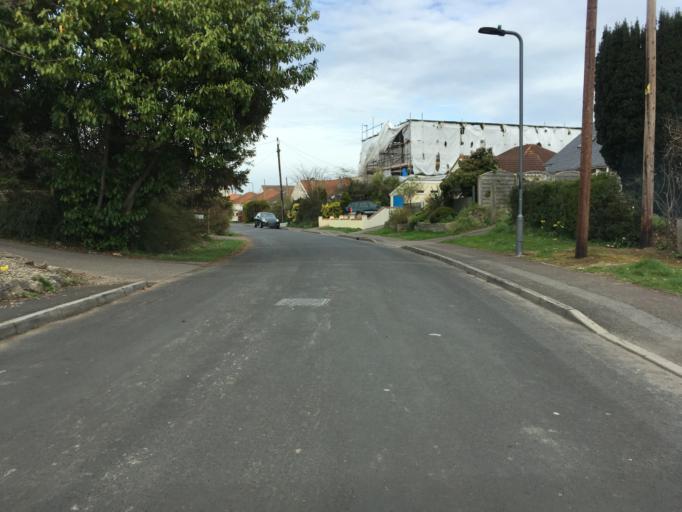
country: GB
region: England
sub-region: South Gloucestershire
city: Severn Beach
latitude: 51.5178
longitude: -2.6206
